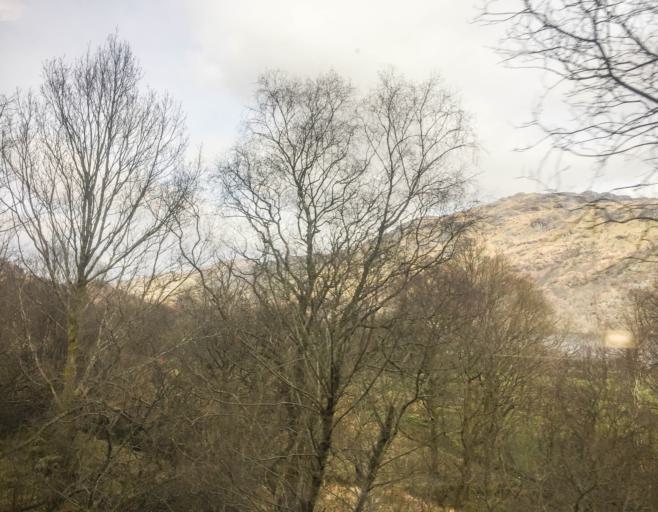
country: GB
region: Scotland
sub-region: Argyll and Bute
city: Garelochhead
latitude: 56.2689
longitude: -4.7071
